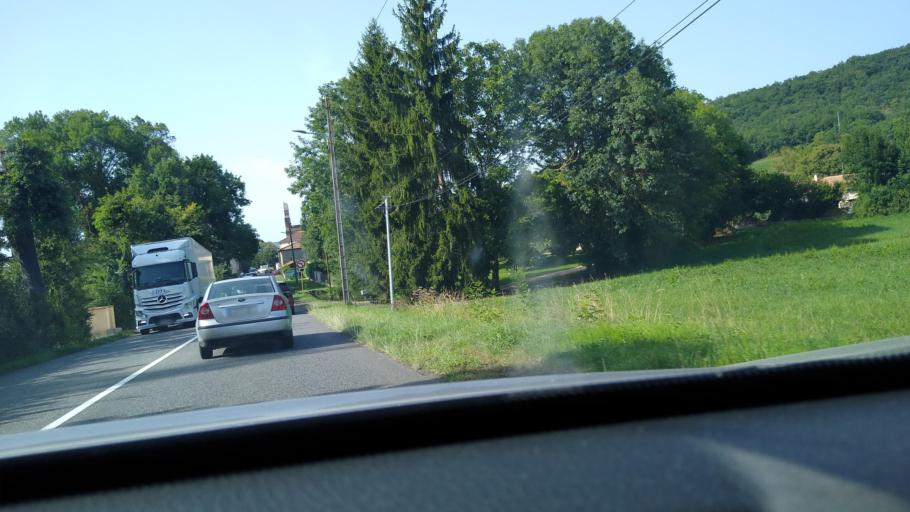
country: FR
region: Midi-Pyrenees
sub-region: Departement de la Haute-Garonne
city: Salies-du-Salat
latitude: 43.1098
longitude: 0.9380
